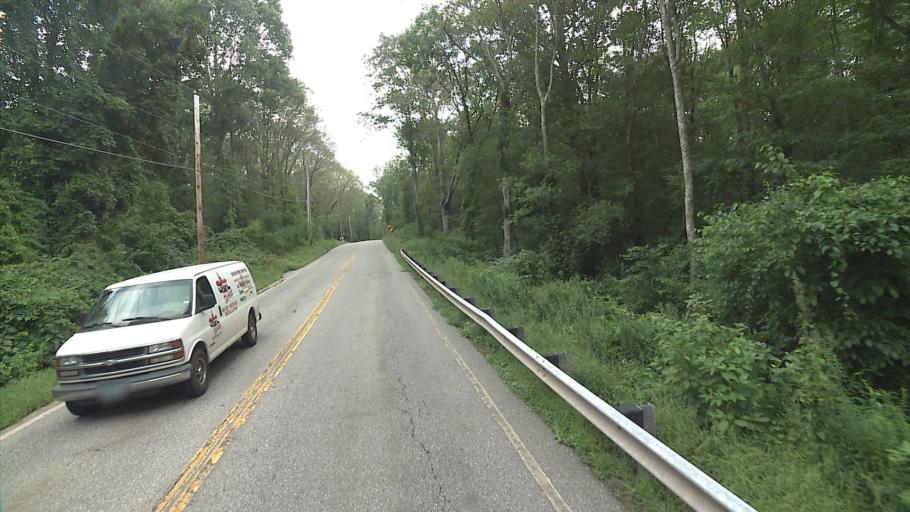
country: US
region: Connecticut
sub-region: New London County
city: Colchester
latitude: 41.4590
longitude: -72.3013
